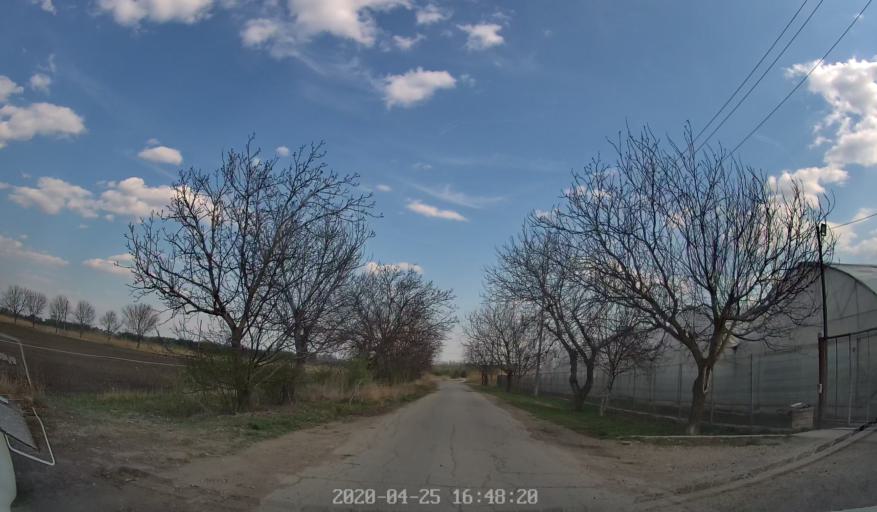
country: MD
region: Chisinau
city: Vadul lui Voda
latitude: 47.1315
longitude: 29.0793
